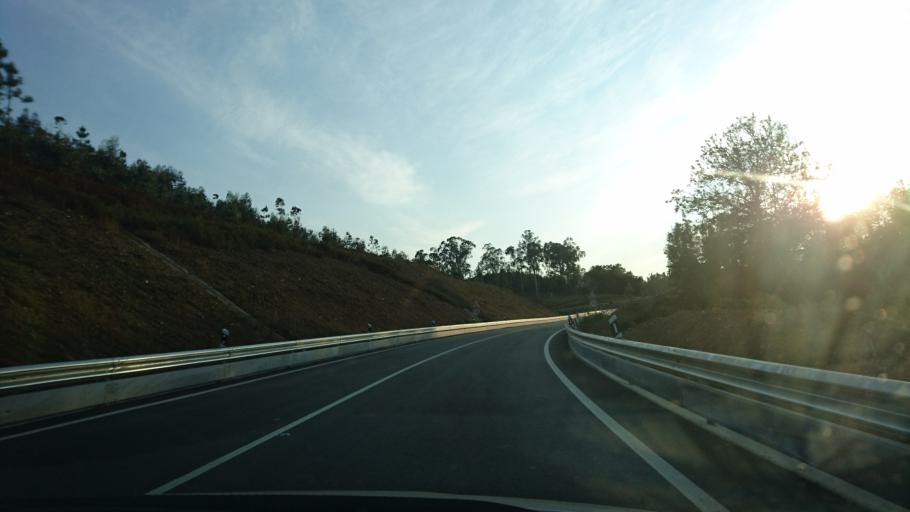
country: PT
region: Vila Real
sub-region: Mondim de Basto
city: Mondim de Basto
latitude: 41.4094
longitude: -7.9797
